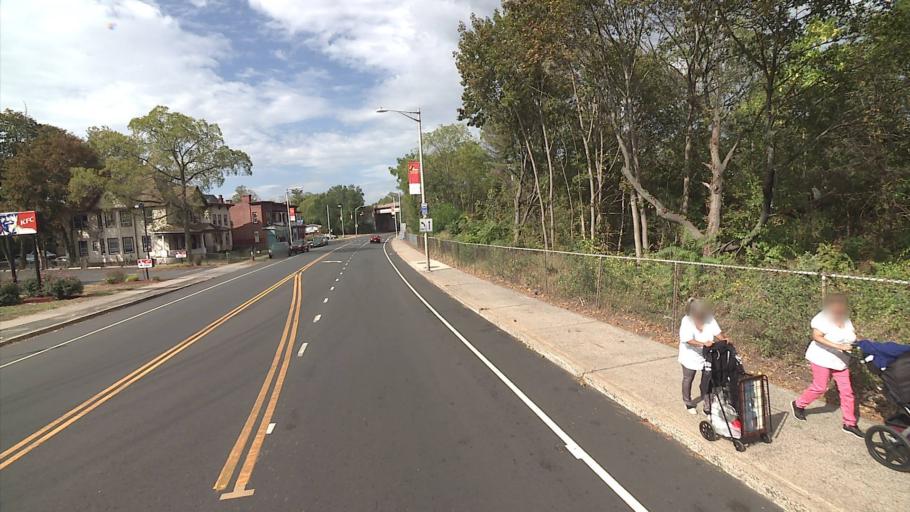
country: US
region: Connecticut
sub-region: Hartford County
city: New Britain
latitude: 41.6653
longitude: -72.7953
